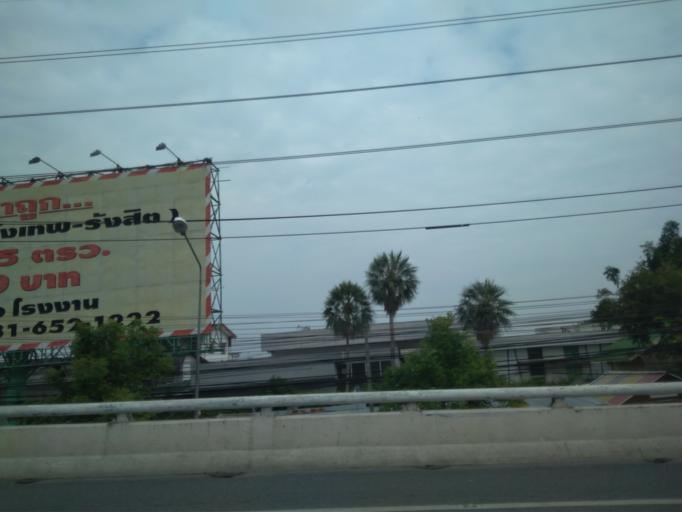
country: TH
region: Bangkok
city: Suan Luang
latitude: 13.7154
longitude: 100.6432
